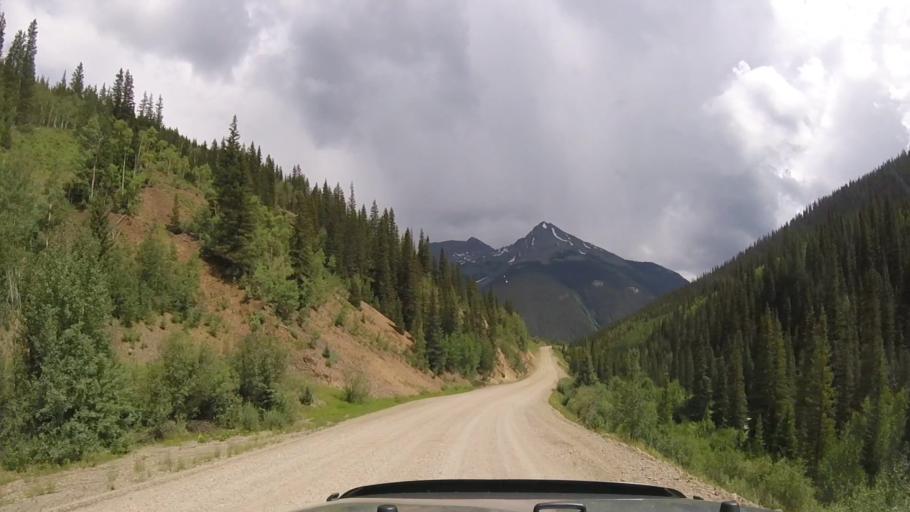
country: US
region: Colorado
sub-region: San Juan County
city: Silverton
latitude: 37.8264
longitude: -107.6681
